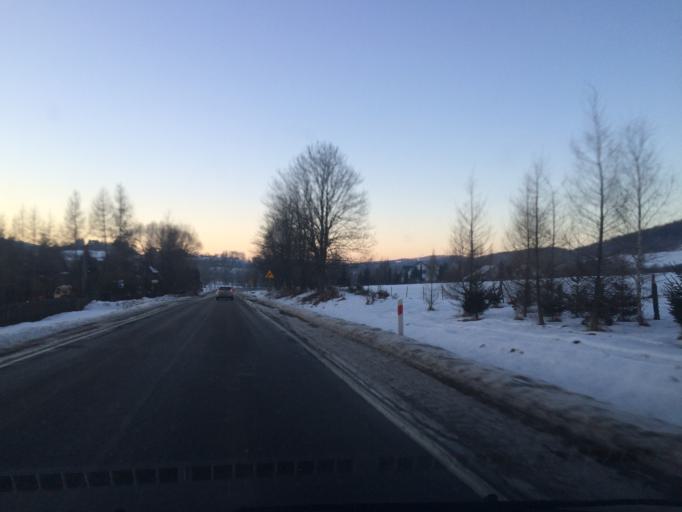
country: PL
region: Subcarpathian Voivodeship
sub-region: Powiat bieszczadzki
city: Czarna
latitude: 49.3725
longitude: 22.6486
